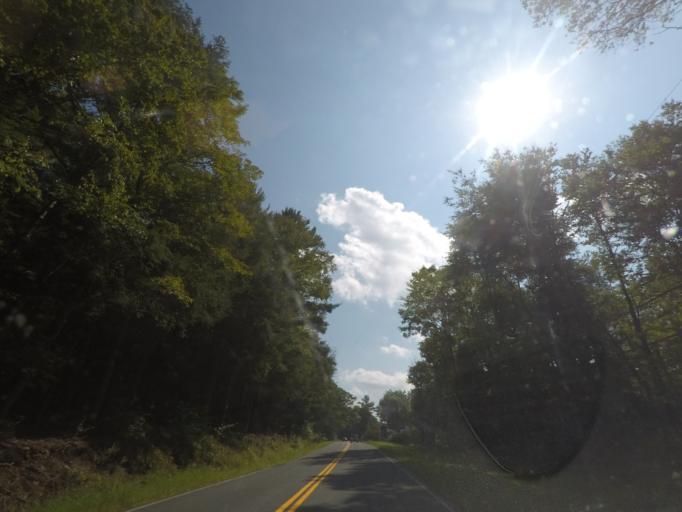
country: US
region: New York
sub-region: Rensselaer County
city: Poestenkill
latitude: 42.6992
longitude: -73.5154
